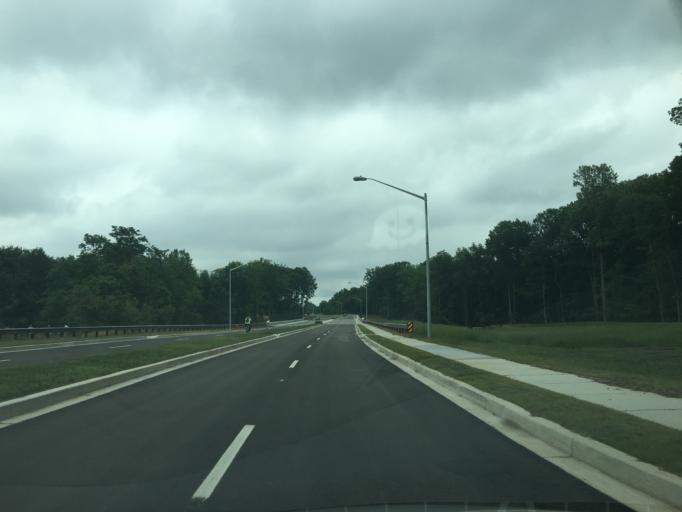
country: US
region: Maryland
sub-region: Baltimore County
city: Randallstown
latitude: 39.3810
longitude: -76.8113
